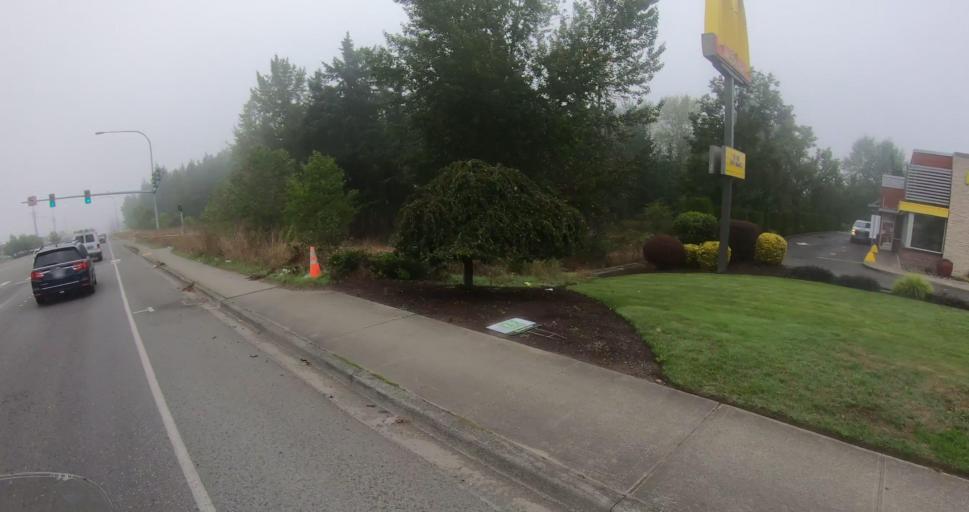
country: US
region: Washington
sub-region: Pierce County
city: Graham
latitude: 47.0996
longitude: -122.2939
